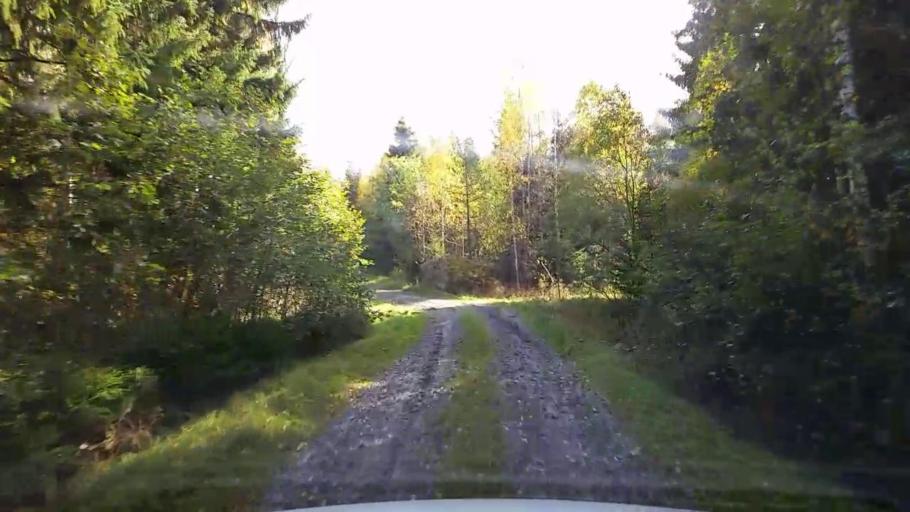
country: SE
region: Gaevleborg
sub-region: Ljusdals Kommun
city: Jaervsoe
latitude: 61.7797
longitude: 16.1834
